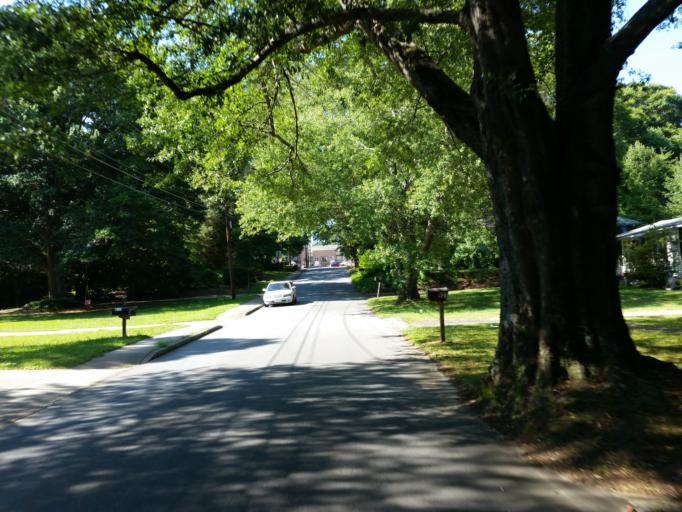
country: US
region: Georgia
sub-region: Fulton County
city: Roswell
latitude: 34.0237
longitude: -84.3558
